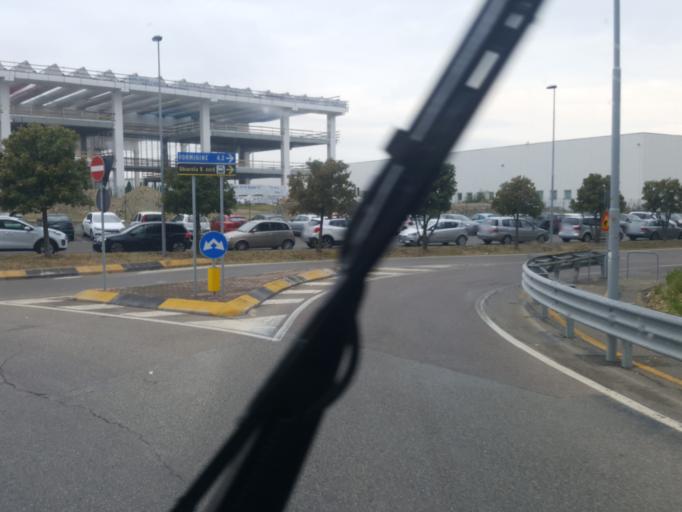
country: IT
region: Emilia-Romagna
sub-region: Provincia di Modena
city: Fiorano
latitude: 44.5525
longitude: 10.8218
